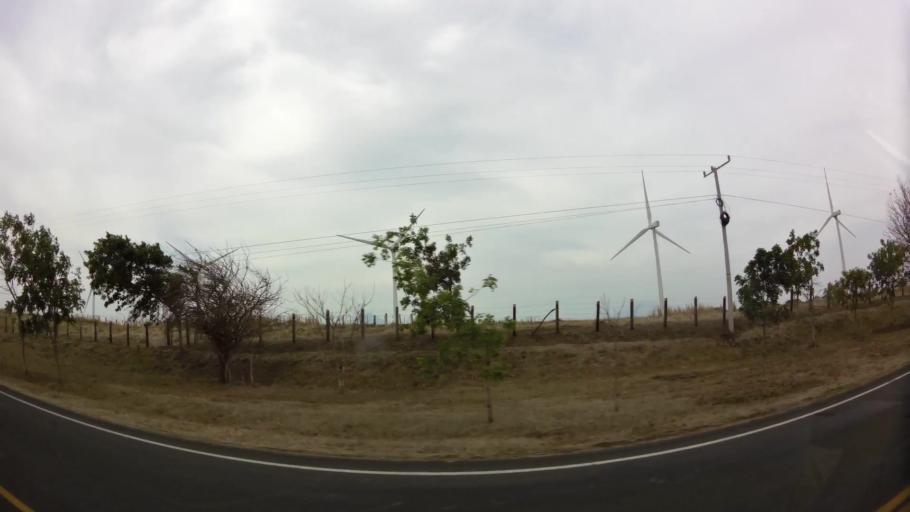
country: NI
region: Rivas
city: Rivas
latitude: 11.3627
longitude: -85.7489
